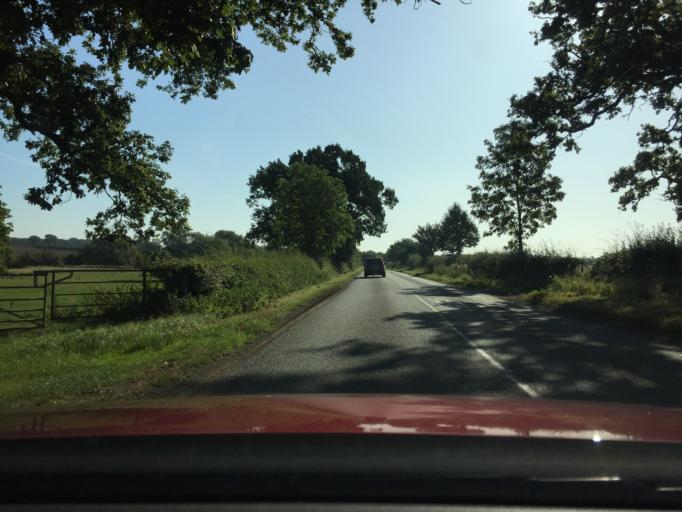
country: GB
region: England
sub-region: Leicestershire
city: Syston
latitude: 52.6767
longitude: -1.0442
